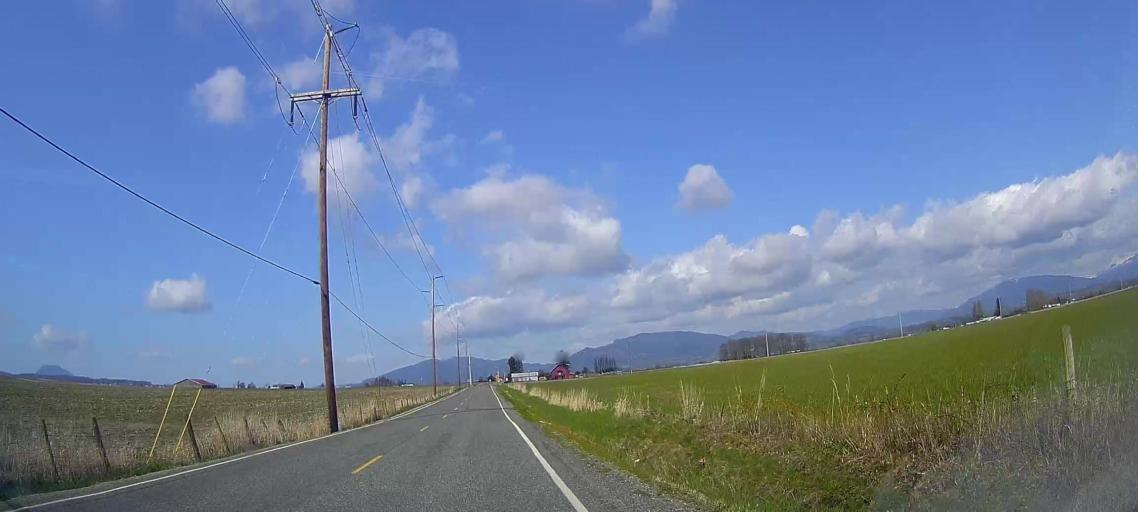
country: US
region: Washington
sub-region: Skagit County
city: Burlington
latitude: 48.5126
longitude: -122.4445
